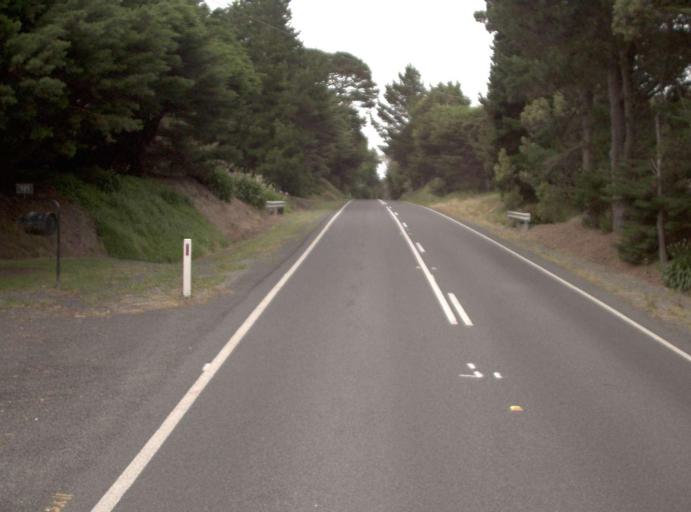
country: AU
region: Victoria
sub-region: Bass Coast
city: North Wonthaggi
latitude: -38.4865
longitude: 145.7500
